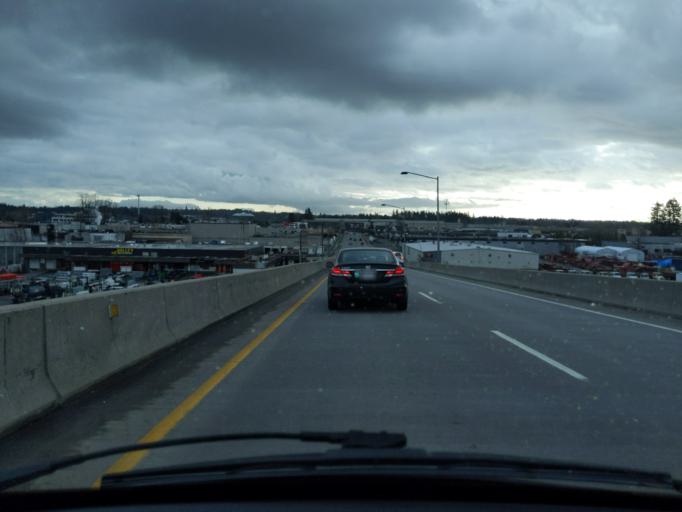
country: CA
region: British Columbia
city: Walnut Grove
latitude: 49.1815
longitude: -122.6693
